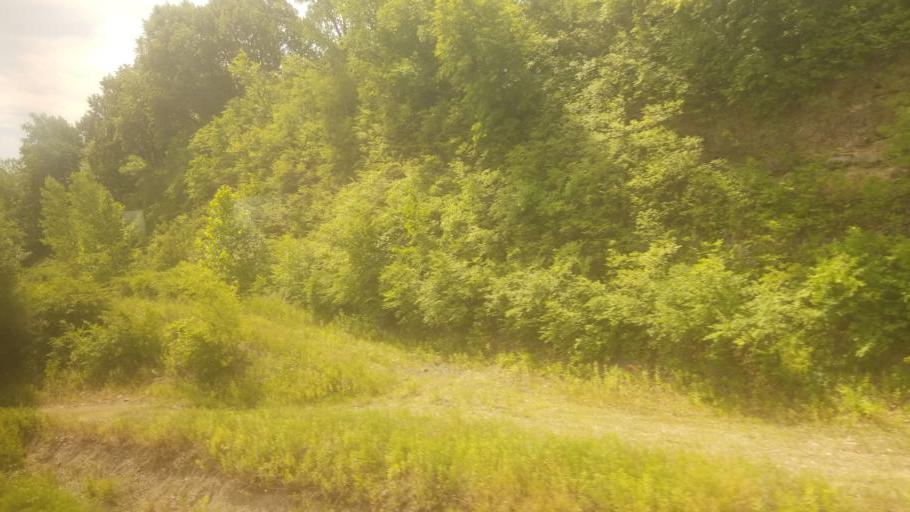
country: US
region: Missouri
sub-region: Jackson County
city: Sugar Creek
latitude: 39.1137
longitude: -94.4826
